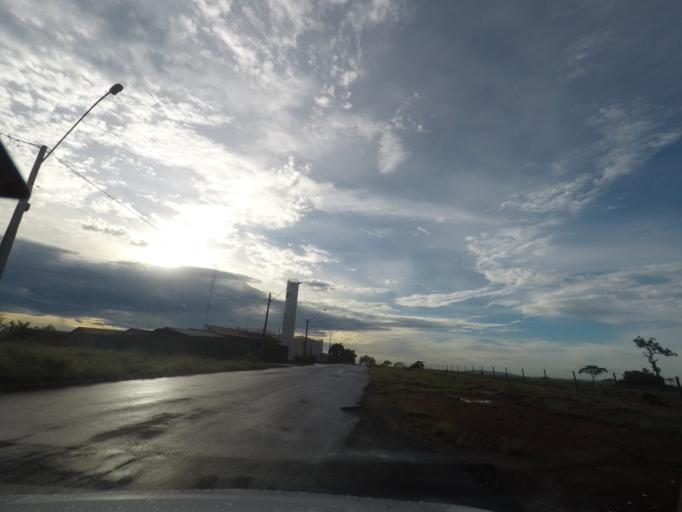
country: BR
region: Goias
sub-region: Goiania
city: Goiania
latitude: -16.7548
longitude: -49.3813
